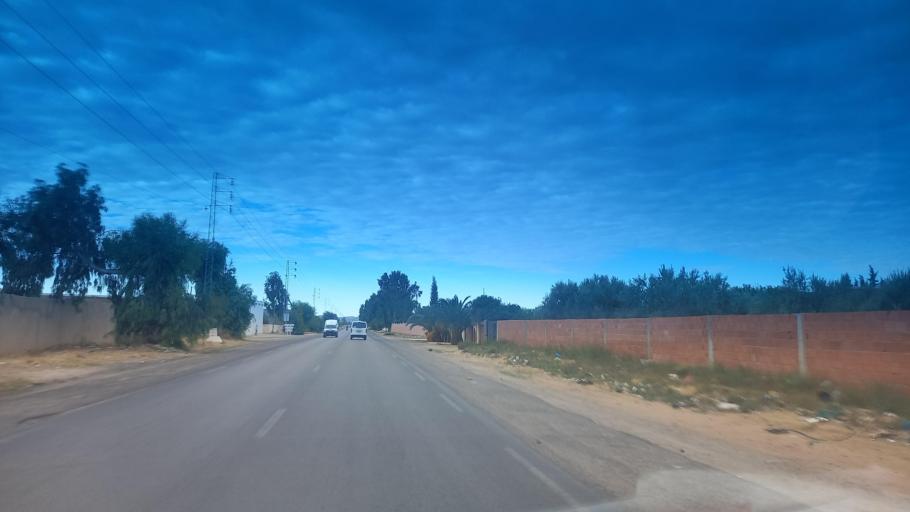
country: TN
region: Al Qasrayn
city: Sbiba
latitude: 35.2687
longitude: 9.0931
